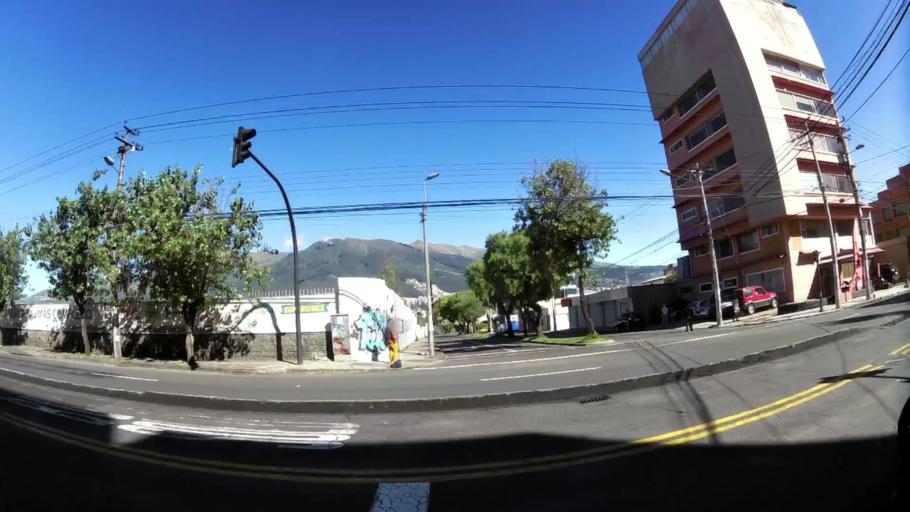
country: EC
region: Pichincha
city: Quito
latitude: -0.1657
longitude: -78.4754
